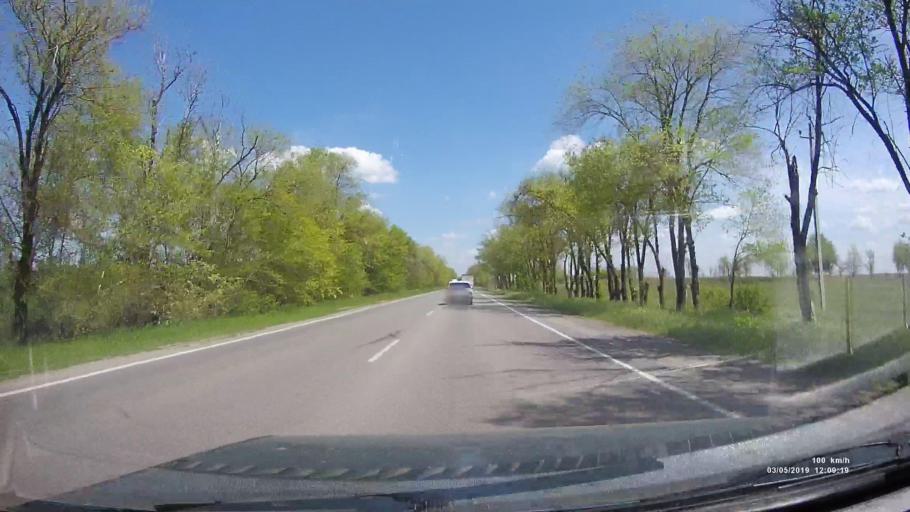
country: RU
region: Rostov
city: Bagayevskaya
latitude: 47.2940
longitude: 40.5141
